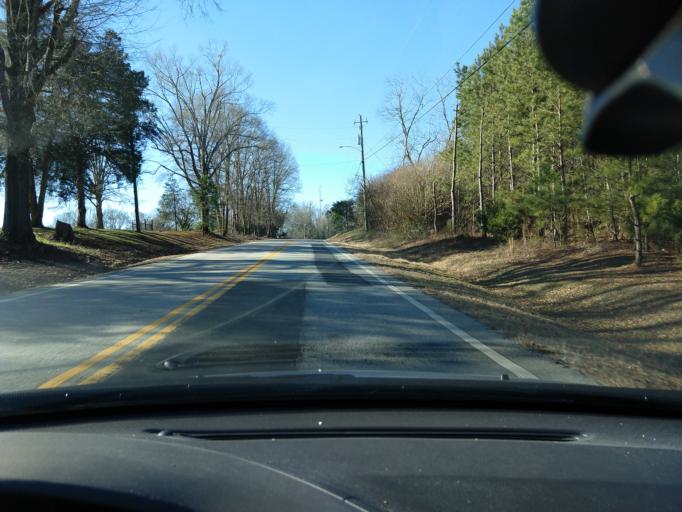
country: US
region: Georgia
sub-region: Barrow County
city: Statham
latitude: 33.9631
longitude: -83.6003
